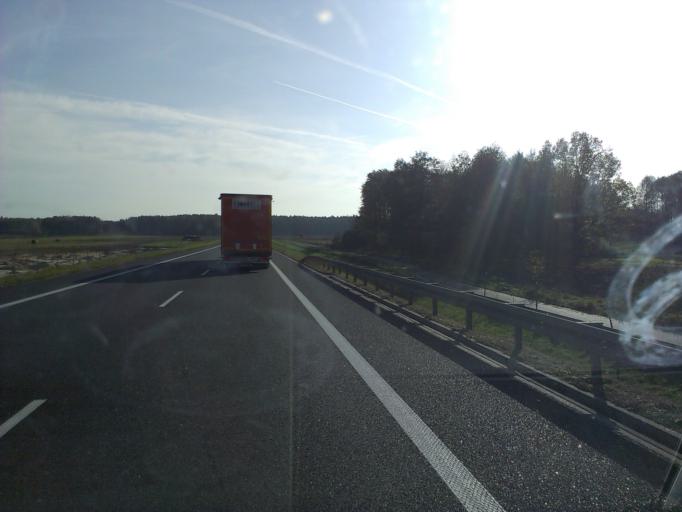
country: PL
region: Lubusz
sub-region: Powiat nowosolski
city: Otyn
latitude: 51.8621
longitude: 15.6630
